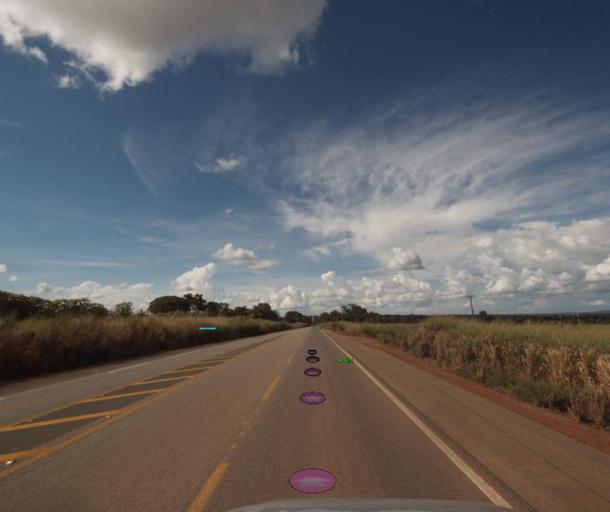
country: BR
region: Goias
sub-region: Porangatu
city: Porangatu
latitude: -13.1019
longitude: -49.1985
